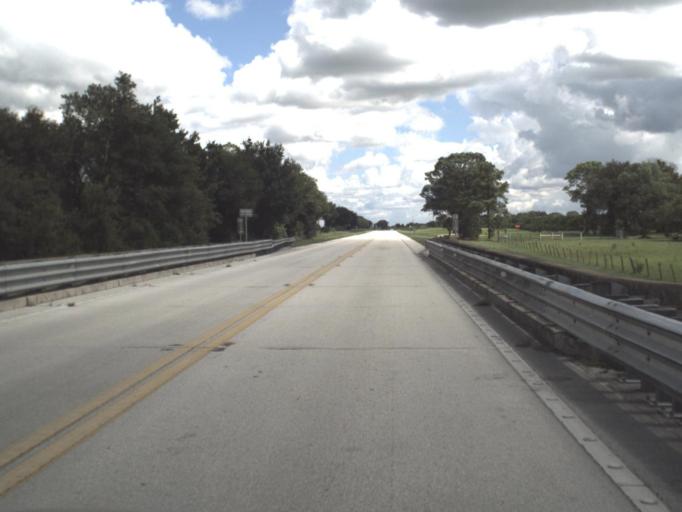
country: US
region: Florida
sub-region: DeSoto County
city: Southeast Arcadia
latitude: 27.2087
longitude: -81.7591
